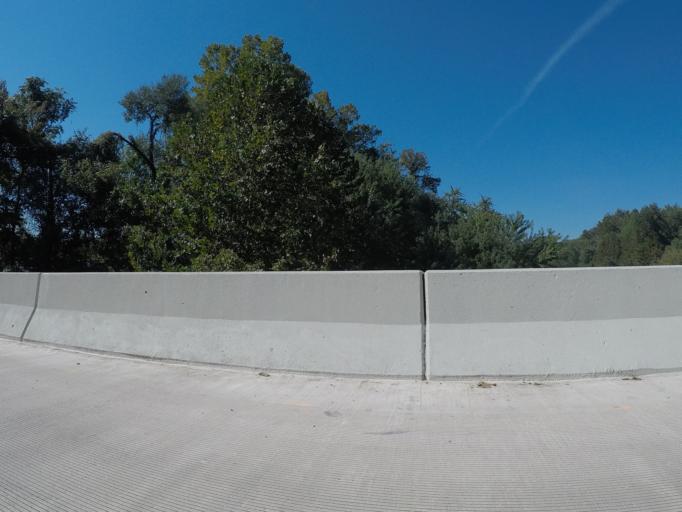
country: US
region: West Virginia
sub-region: Cabell County
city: Pea Ridge
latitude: 38.4131
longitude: -82.3611
